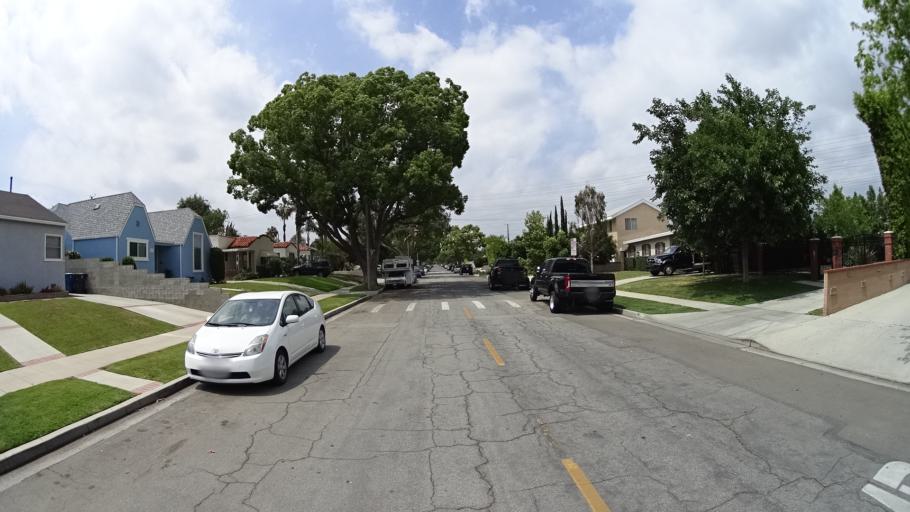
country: US
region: California
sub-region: Los Angeles County
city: Universal City
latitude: 34.1575
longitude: -118.3373
